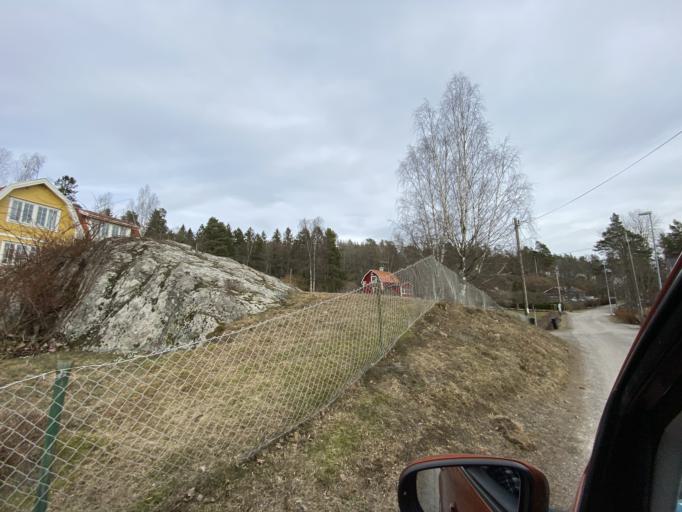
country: SE
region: Stockholm
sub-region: Salems Kommun
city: Ronninge
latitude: 59.2003
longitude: 17.7381
